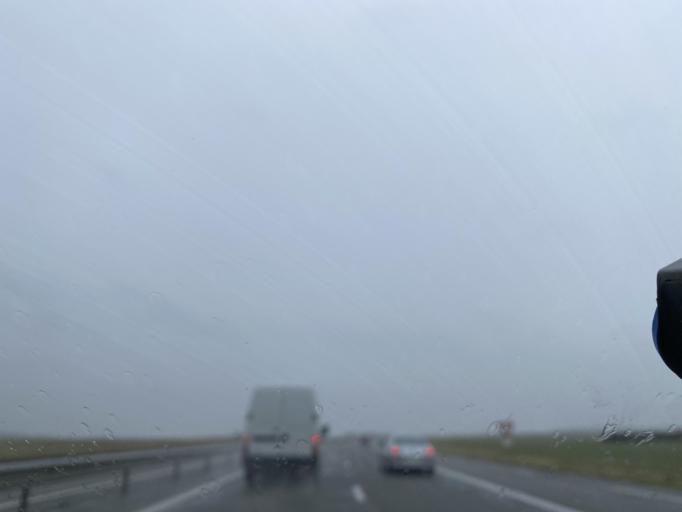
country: FR
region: Centre
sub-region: Departement d'Eure-et-Loir
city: Villemeux-sur-Eure
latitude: 48.6412
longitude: 1.4059
